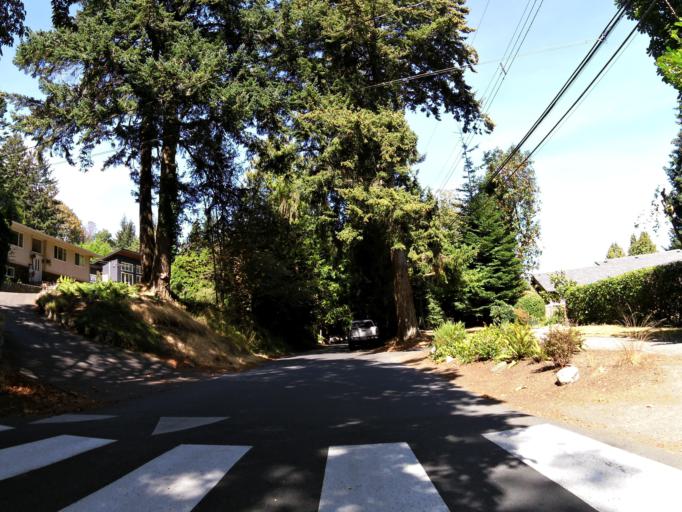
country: CA
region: British Columbia
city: Victoria
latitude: 48.5235
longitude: -123.3724
